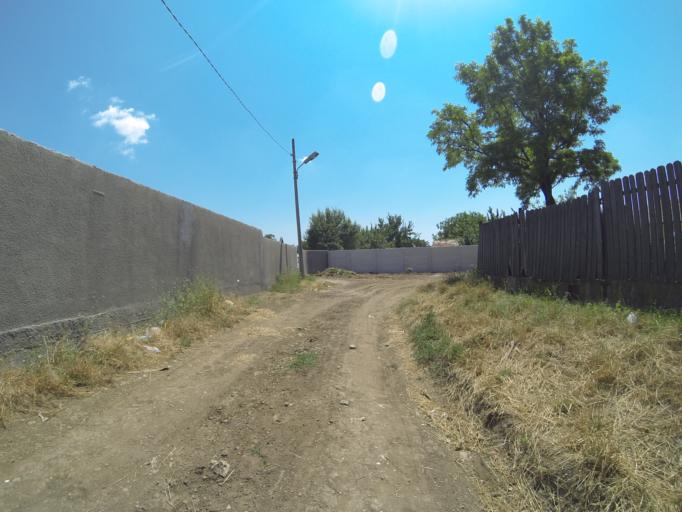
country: RO
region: Dolj
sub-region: Comuna Segarcea
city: Segarcea
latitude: 44.0911
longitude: 23.7537
